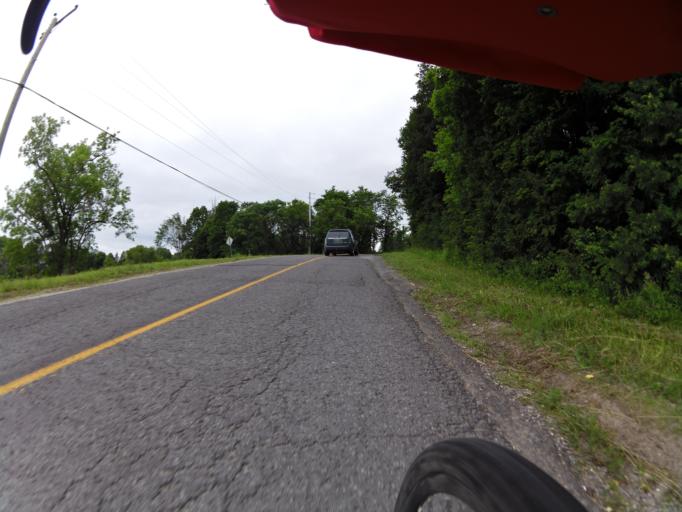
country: CA
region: Quebec
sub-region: Outaouais
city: Wakefield
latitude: 45.7092
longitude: -75.9618
